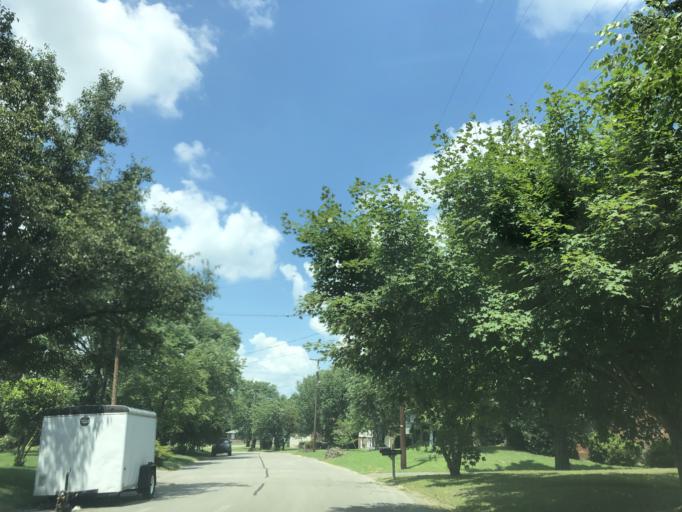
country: US
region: Tennessee
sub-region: Davidson County
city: Lakewood
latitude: 36.1949
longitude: -86.6131
